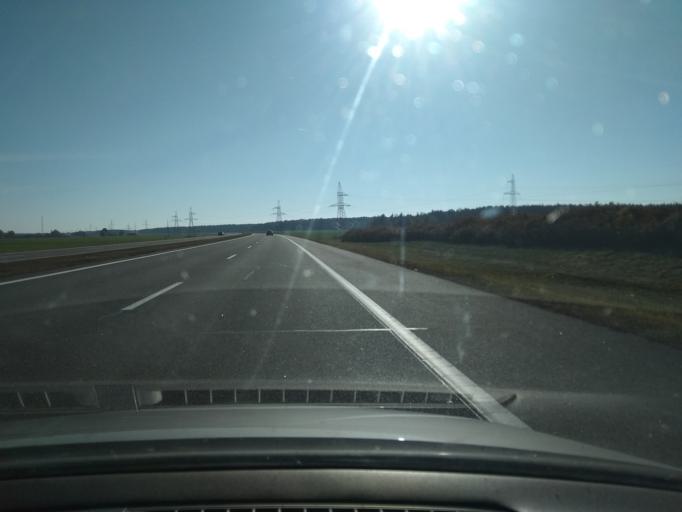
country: BY
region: Brest
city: Baranovichi
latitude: 53.1069
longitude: 25.8893
